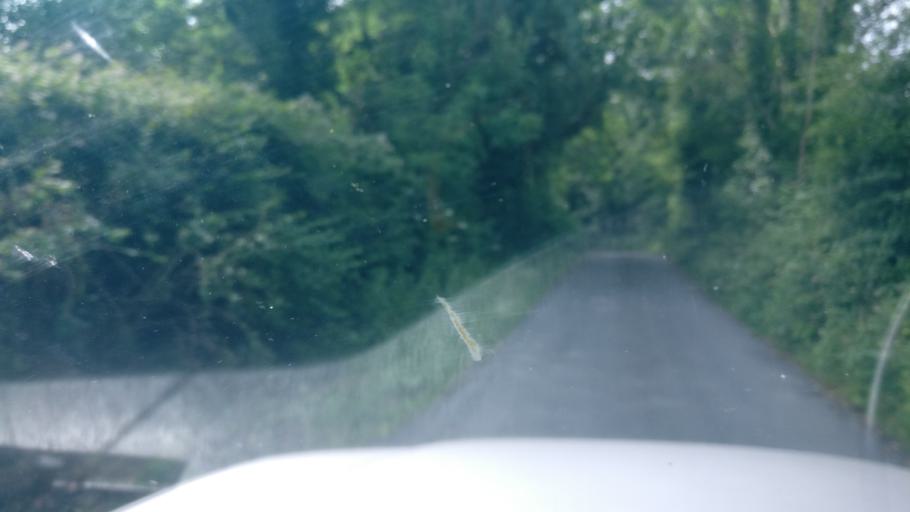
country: IE
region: Connaught
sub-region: County Galway
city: Gort
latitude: 53.1024
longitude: -8.7059
